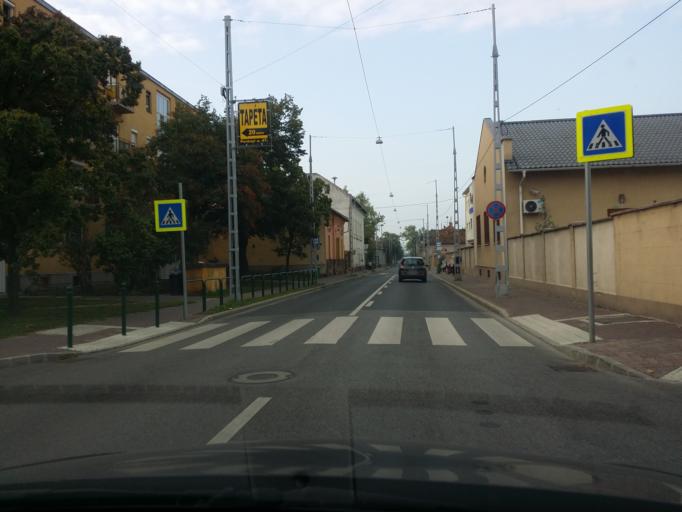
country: HU
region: Budapest
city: Budapest IV. keruelet
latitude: 47.5704
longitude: 19.0859
